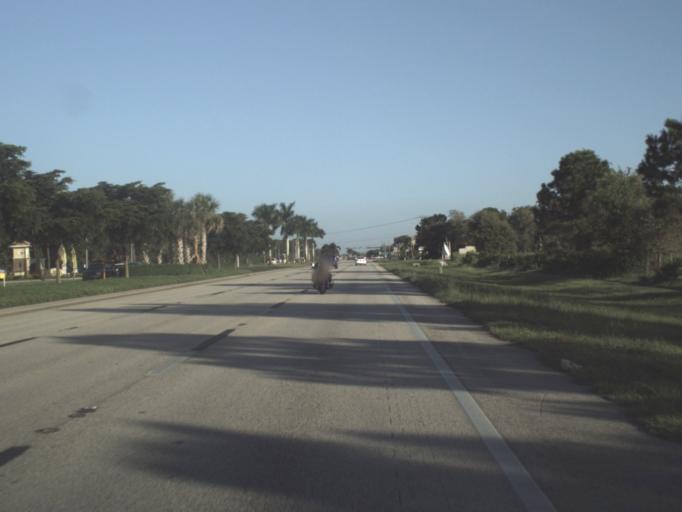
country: US
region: Florida
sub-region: Lee County
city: San Carlos Park
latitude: 26.4718
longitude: -81.8354
